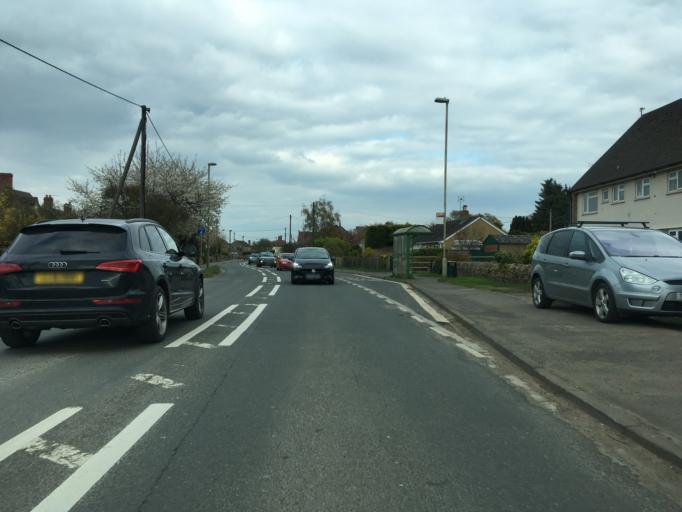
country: GB
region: England
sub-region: Oxfordshire
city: Stonesfield
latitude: 51.8243
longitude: -1.3931
